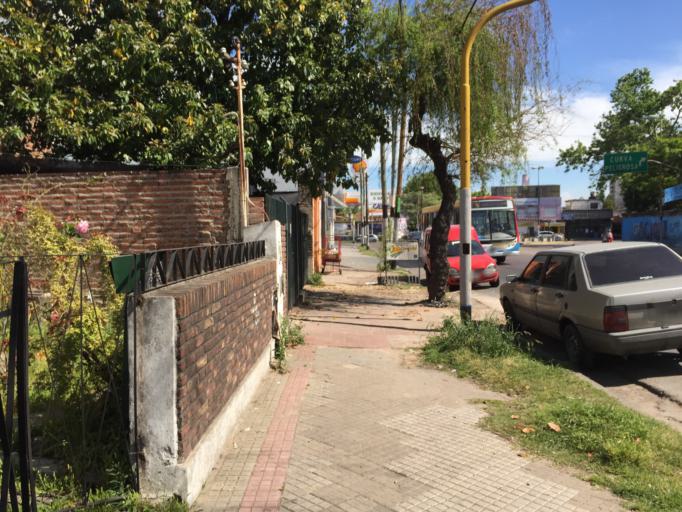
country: AR
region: Buenos Aires
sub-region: Partido de Lomas de Zamora
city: Lomas de Zamora
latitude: -34.7356
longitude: -58.3900
